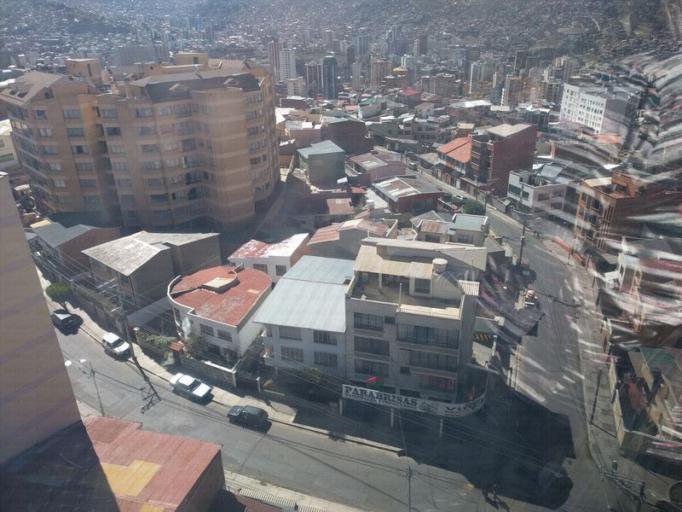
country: BO
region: La Paz
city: La Paz
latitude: -16.5147
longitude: -68.1334
